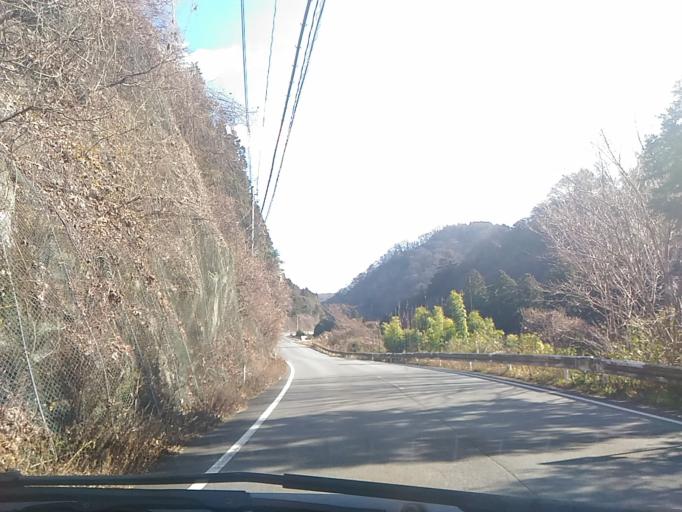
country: JP
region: Fukushima
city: Iwaki
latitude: 37.0028
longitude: 140.7040
